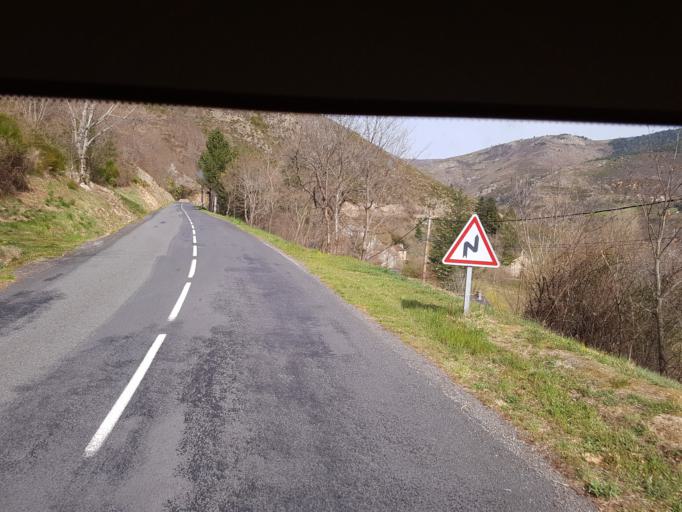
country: FR
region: Languedoc-Roussillon
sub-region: Departement de la Lozere
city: Florac
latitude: 44.3562
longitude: 3.6534
